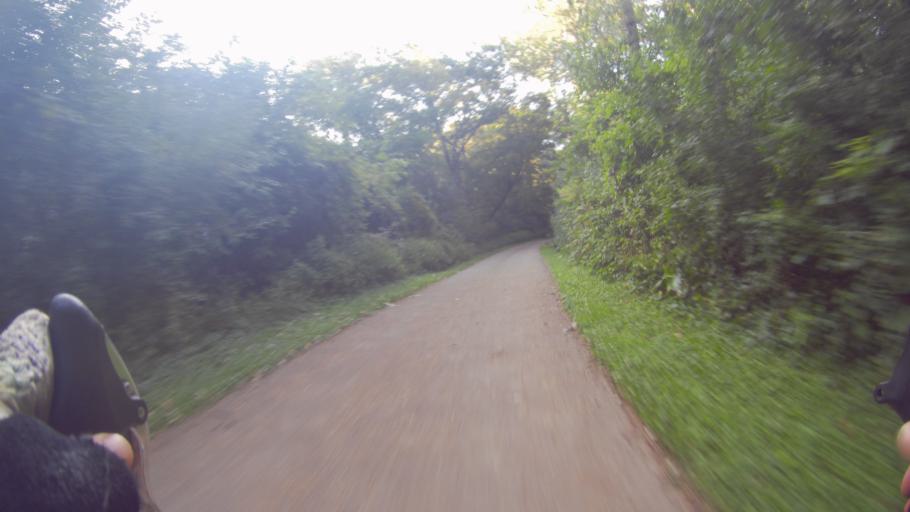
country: US
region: Wisconsin
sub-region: Dane County
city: Madison
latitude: 43.0194
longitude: -89.4262
